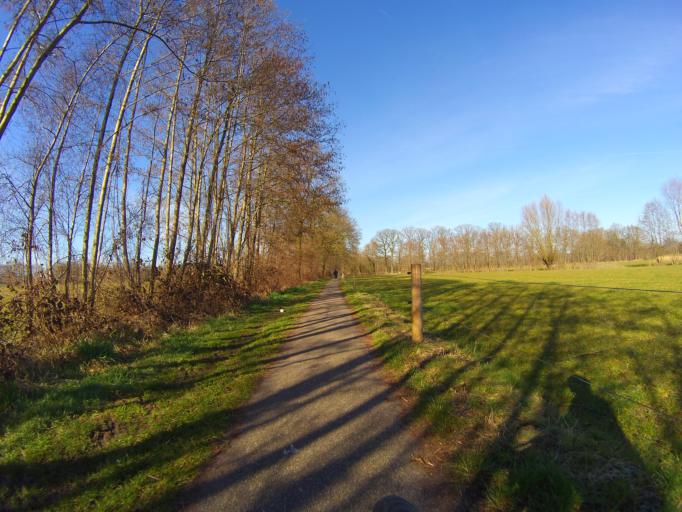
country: NL
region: Utrecht
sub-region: Gemeente Utrechtse Heuvelrug
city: Overberg
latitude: 52.0658
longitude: 5.4926
